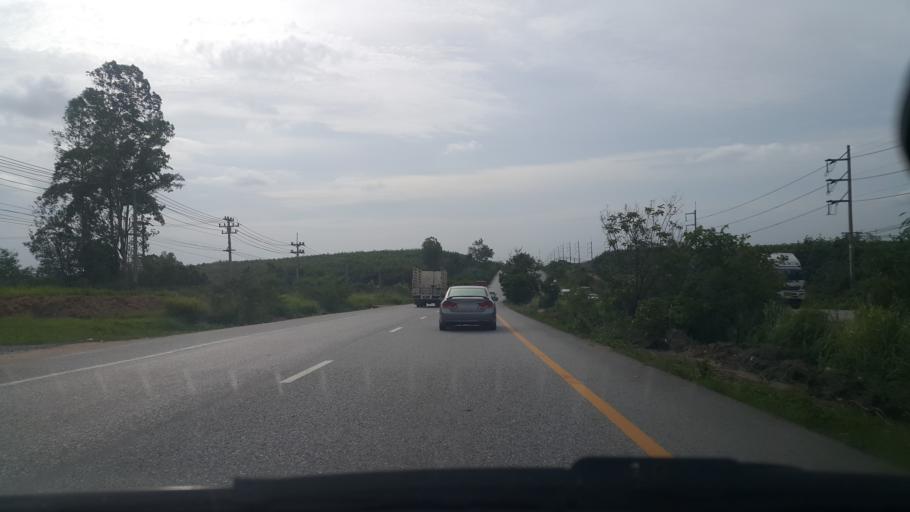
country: TH
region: Rayong
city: Nikhom Phattana
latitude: 12.8710
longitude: 101.0663
